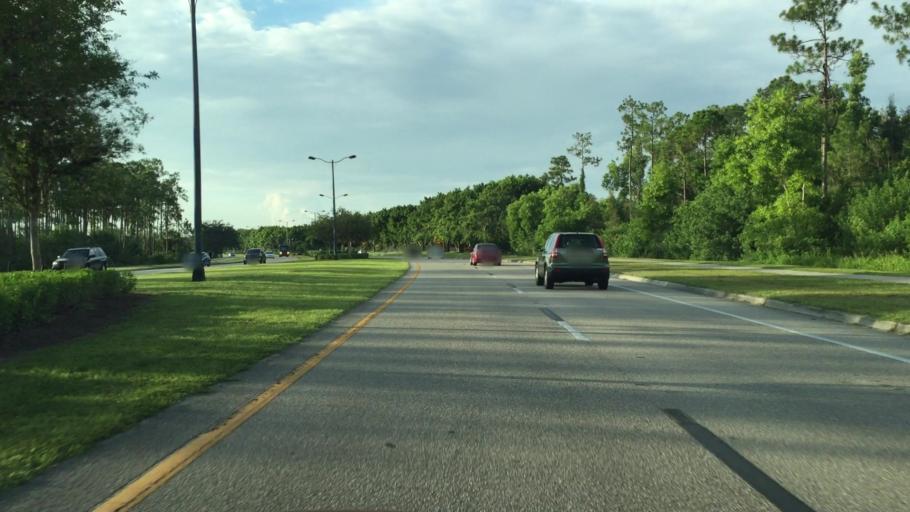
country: US
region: Florida
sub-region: Lee County
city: Three Oaks
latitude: 26.4592
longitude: -81.7831
